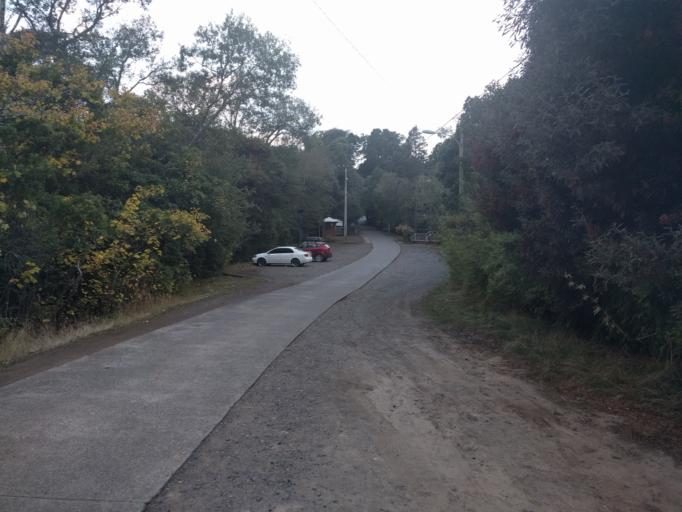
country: CL
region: Araucania
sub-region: Provincia de Cautin
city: Temuco
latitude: -38.7250
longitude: -72.5903
